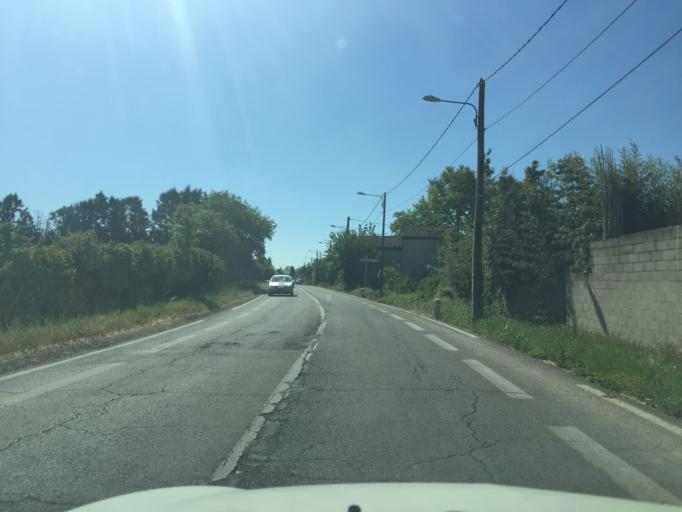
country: FR
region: Provence-Alpes-Cote d'Azur
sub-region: Departement du Vaucluse
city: Le Pontet
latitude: 43.9474
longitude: 4.8615
